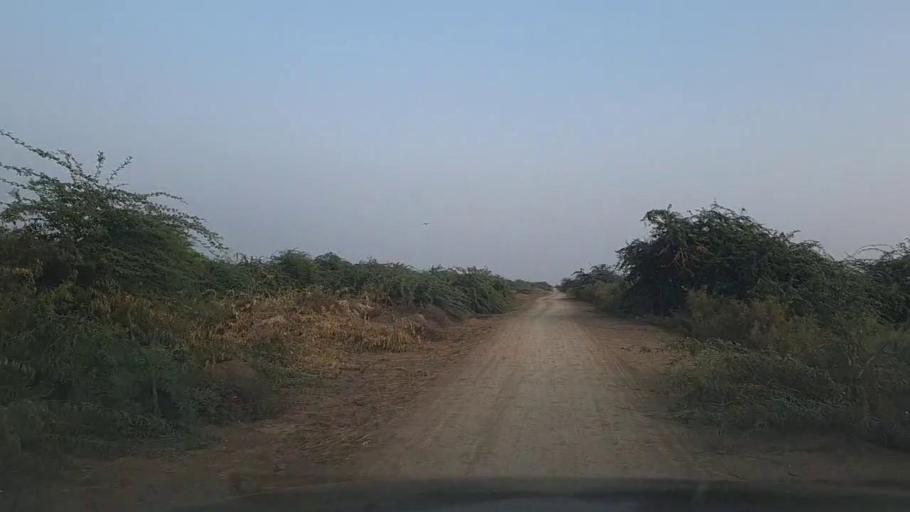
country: PK
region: Sindh
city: Mirpur Batoro
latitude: 24.5455
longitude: 68.3903
